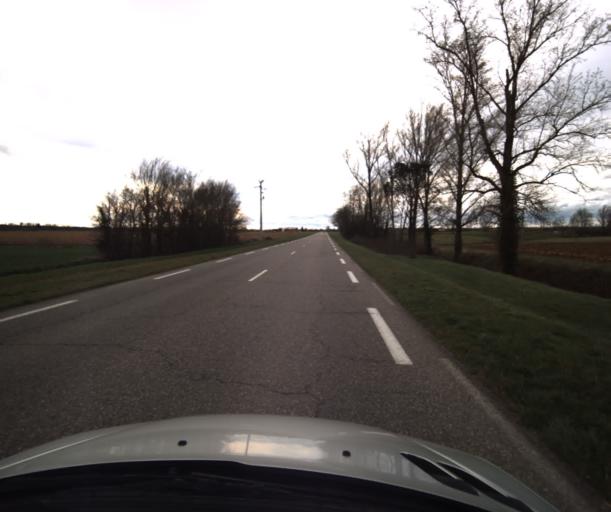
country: FR
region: Midi-Pyrenees
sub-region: Departement du Tarn-et-Garonne
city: Negrepelisse
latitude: 44.0734
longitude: 1.5674
